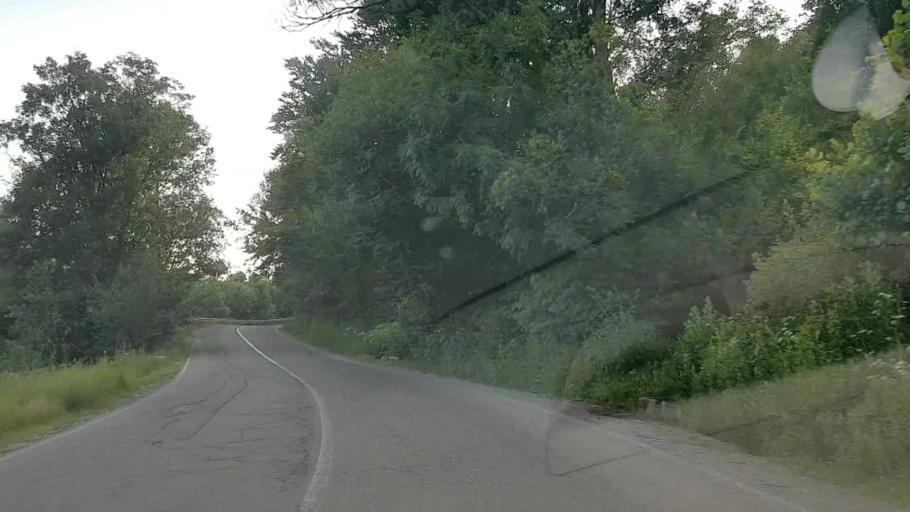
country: RO
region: Harghita
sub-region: Comuna Praid
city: Ocna de Sus
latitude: 46.5714
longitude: 25.1938
